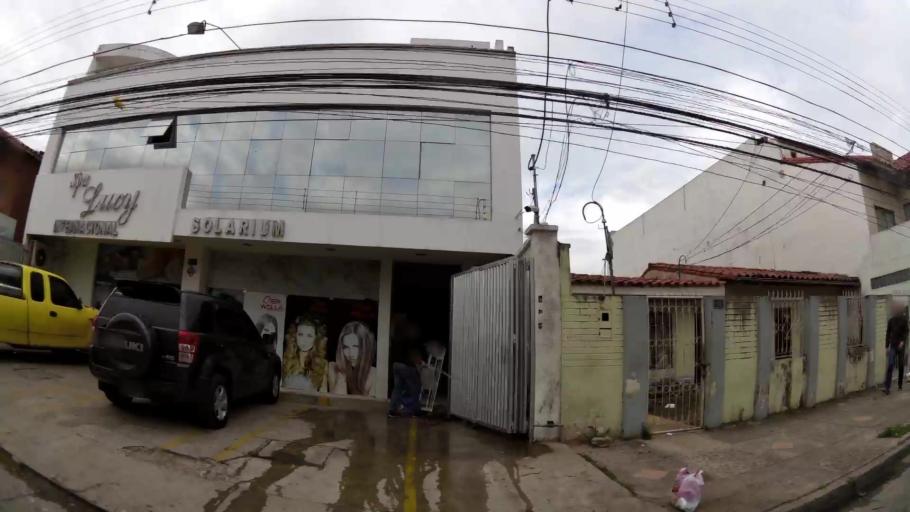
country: BO
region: Santa Cruz
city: Santa Cruz de la Sierra
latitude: -17.7654
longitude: -63.1642
